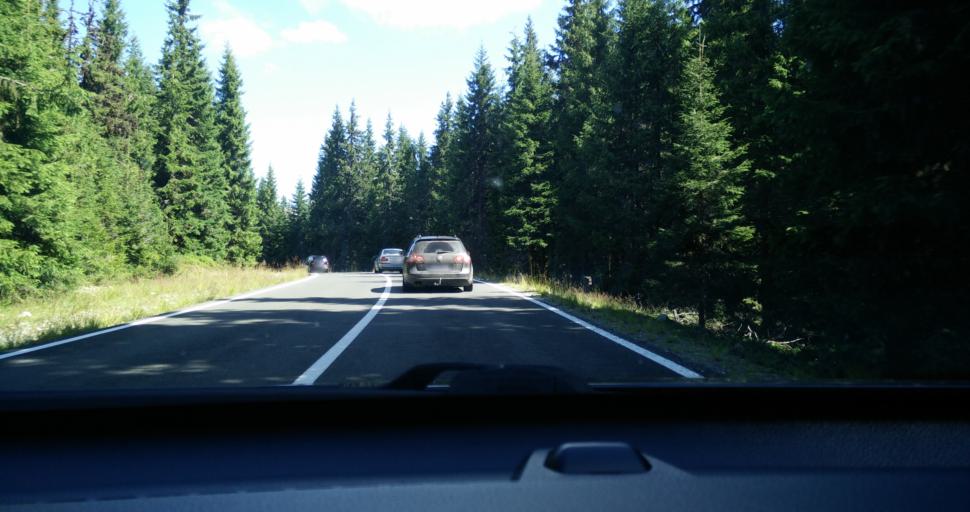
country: RO
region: Hunedoara
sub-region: Oras Petrila
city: Petrila
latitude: 45.4696
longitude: 23.6335
